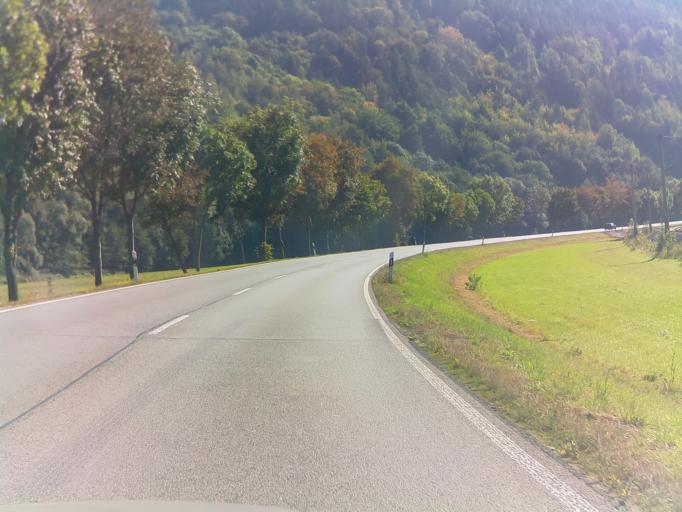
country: DE
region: Thuringia
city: Kaulsdorf
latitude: 50.6058
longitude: 11.4428
